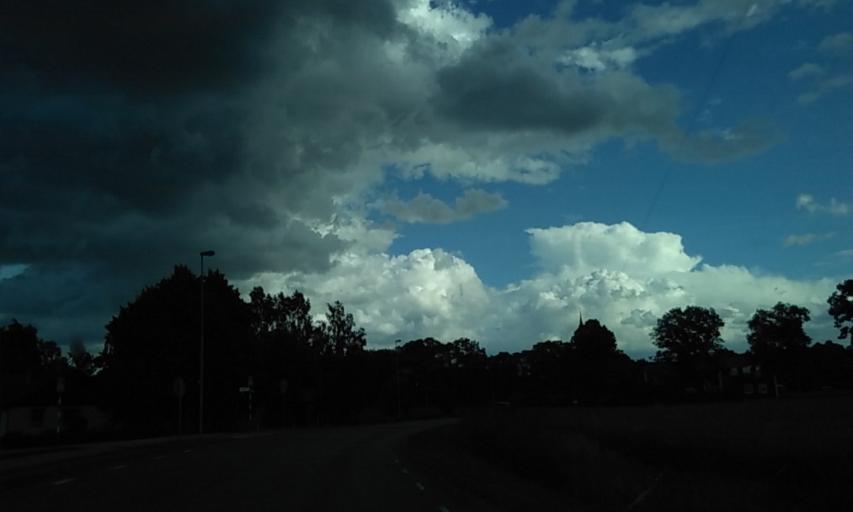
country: SE
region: Vaestra Goetaland
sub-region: Lidkopings Kommun
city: Lidkoping
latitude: 58.5100
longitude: 13.0042
